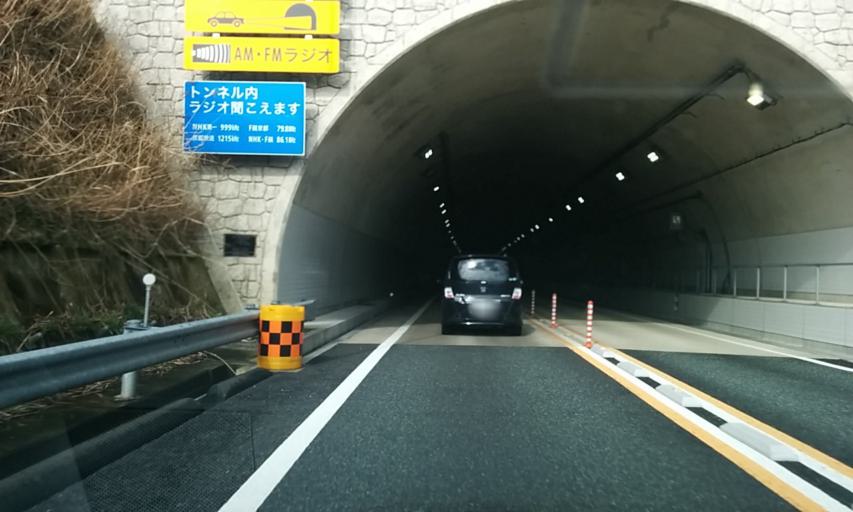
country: JP
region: Kyoto
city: Miyazu
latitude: 35.5530
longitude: 135.1334
